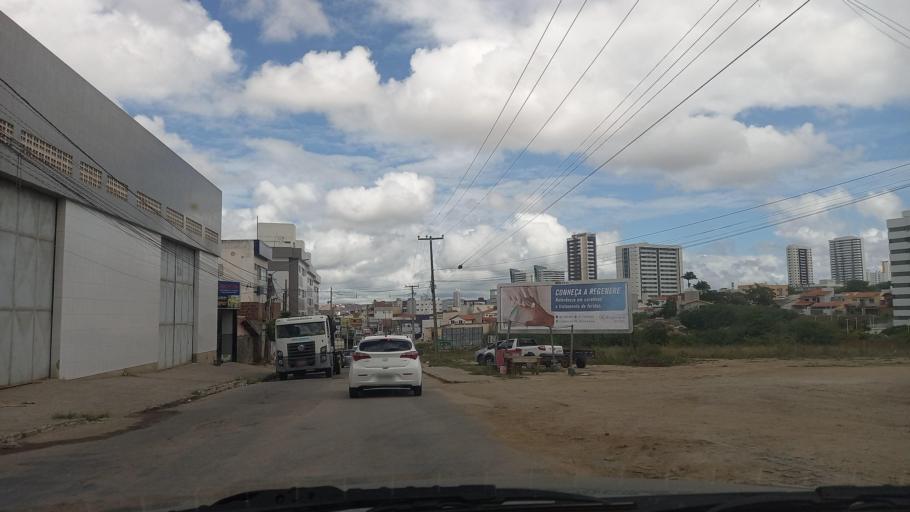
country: BR
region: Pernambuco
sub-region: Caruaru
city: Caruaru
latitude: -8.2653
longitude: -35.9607
